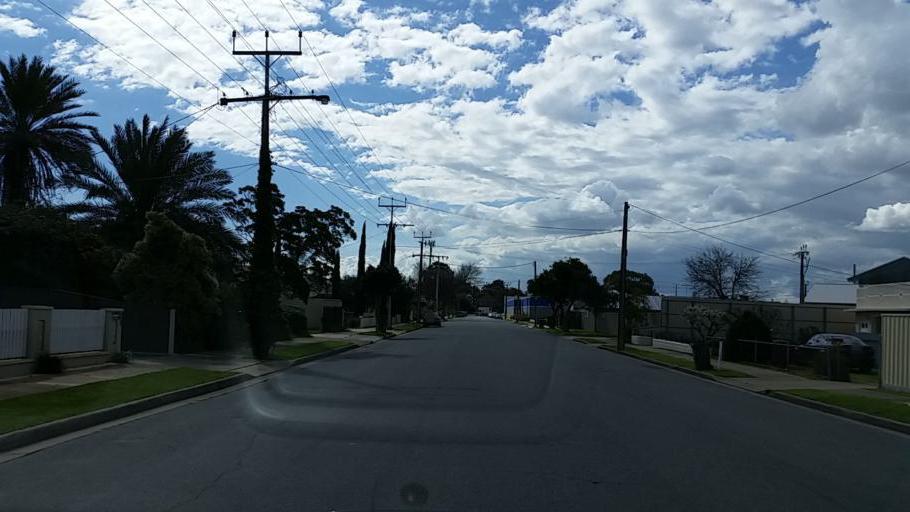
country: AU
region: South Australia
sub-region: Charles Sturt
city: Albert Park
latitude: -34.8776
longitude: 138.5254
